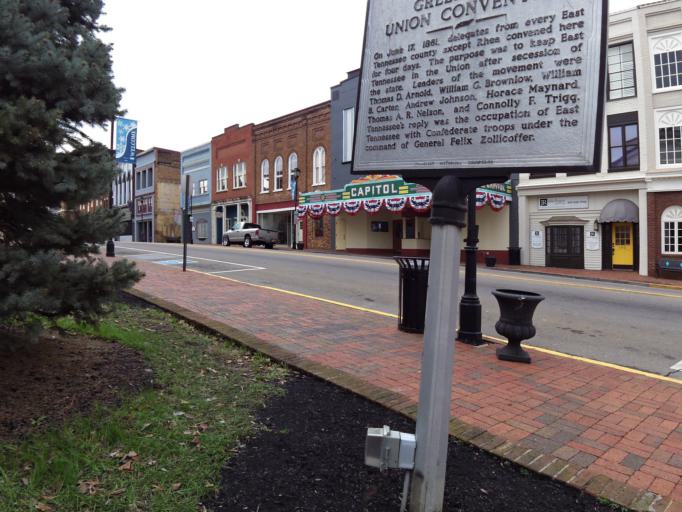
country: US
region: Tennessee
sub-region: Greene County
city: Greeneville
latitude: 36.1631
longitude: -82.8308
